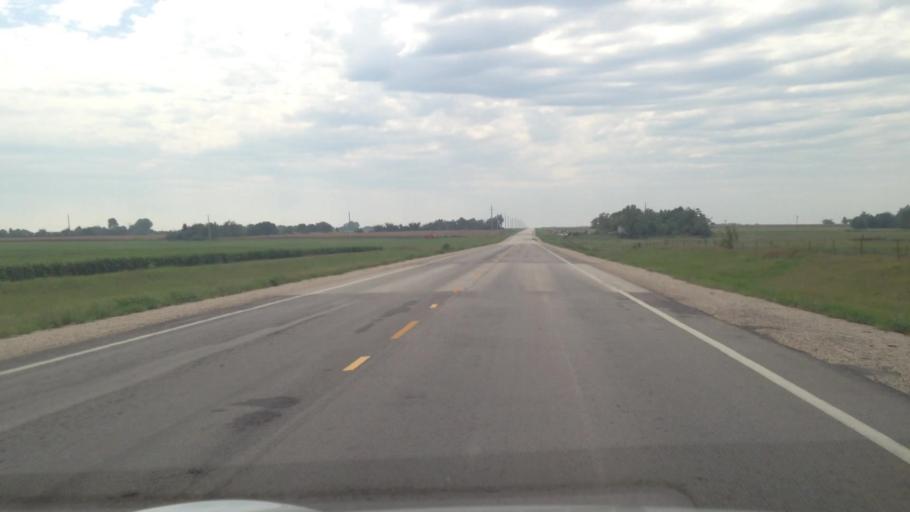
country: US
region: Kansas
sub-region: Anderson County
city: Garnett
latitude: 38.0719
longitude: -95.1694
